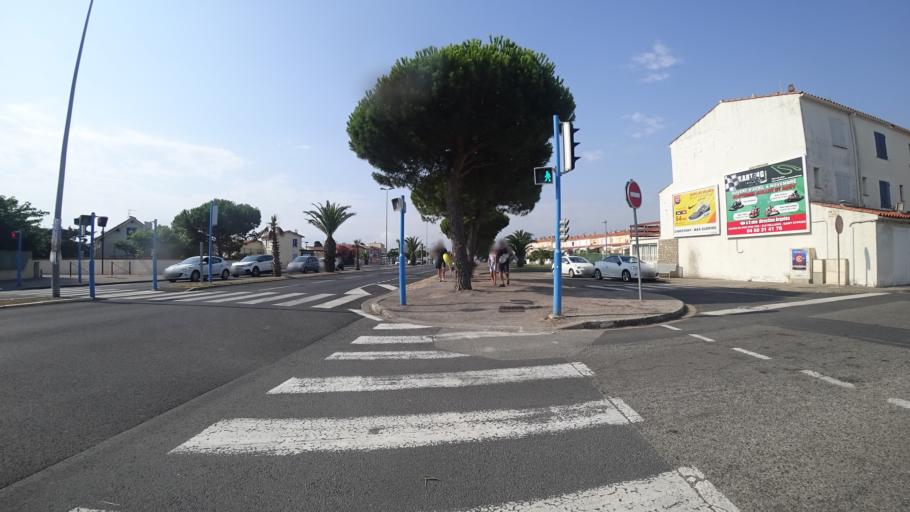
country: FR
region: Languedoc-Roussillon
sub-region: Departement des Pyrenees-Orientales
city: Saint-Cyprien-Plage
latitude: 42.6348
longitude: 3.0331
